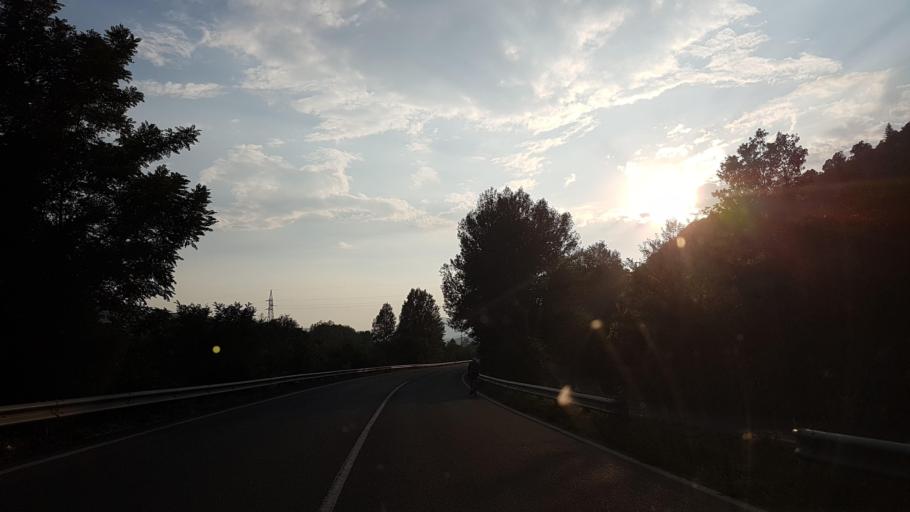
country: IT
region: Emilia-Romagna
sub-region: Provincia di Parma
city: Borgo Val di Taro
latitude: 44.4977
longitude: 9.7992
